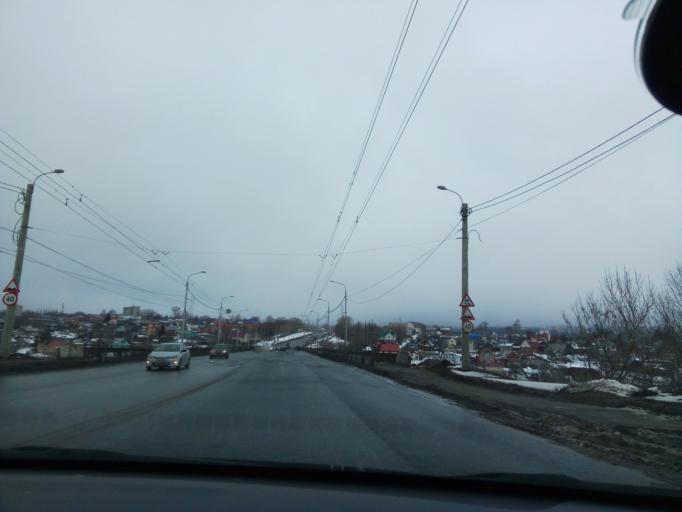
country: RU
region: Chuvashia
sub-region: Cheboksarskiy Rayon
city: Cheboksary
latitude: 56.1251
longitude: 47.2217
